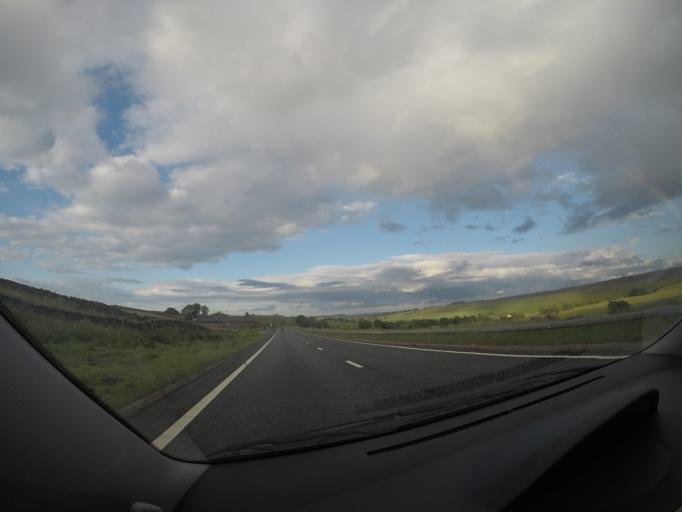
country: GB
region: England
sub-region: County Durham
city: Bowes
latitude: 54.5122
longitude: -2.0636
